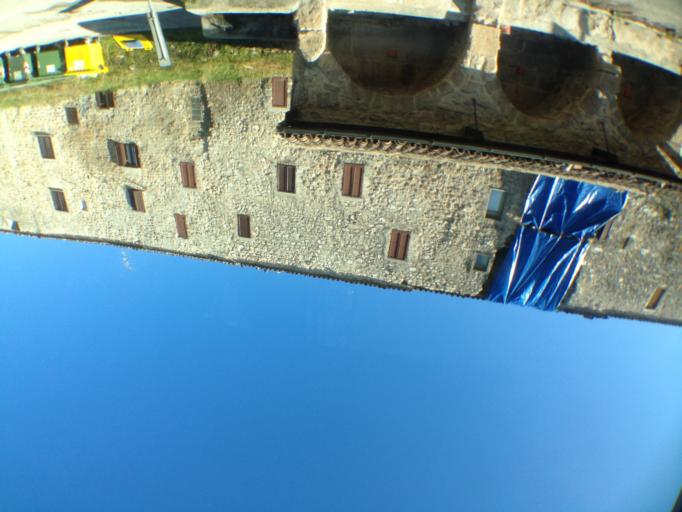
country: IT
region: Umbria
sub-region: Provincia di Perugia
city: Norcia
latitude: 42.7943
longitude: 13.0979
